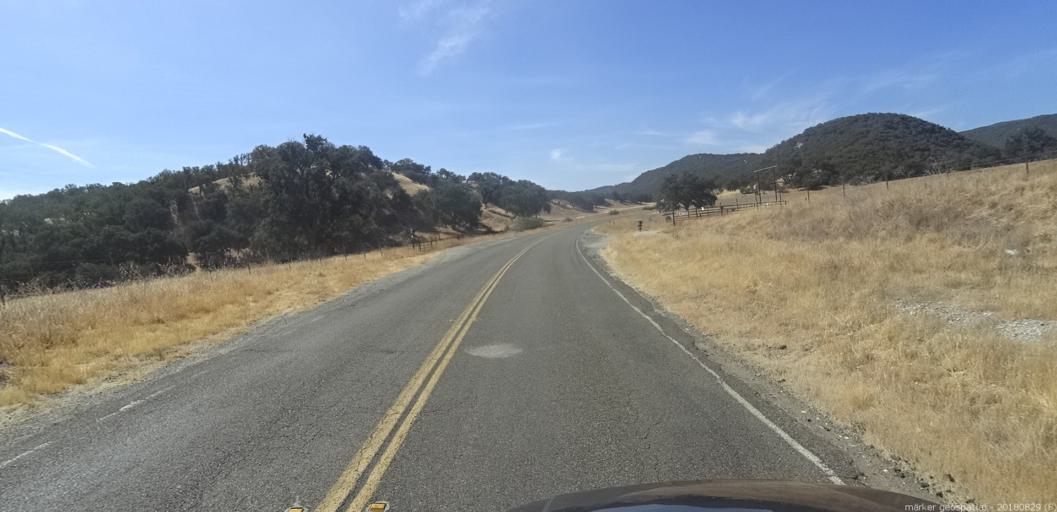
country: US
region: California
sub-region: San Luis Obispo County
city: Lake Nacimiento
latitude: 35.8846
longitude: -121.0657
